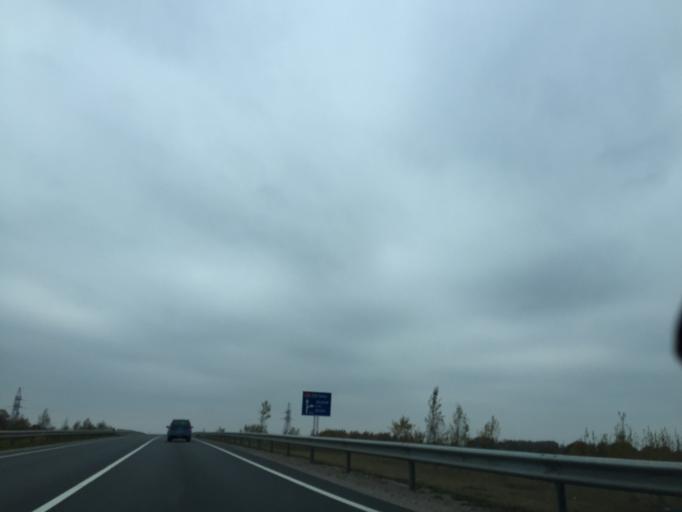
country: LV
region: Ozolnieku
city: Ozolnieki
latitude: 56.6540
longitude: 23.8031
